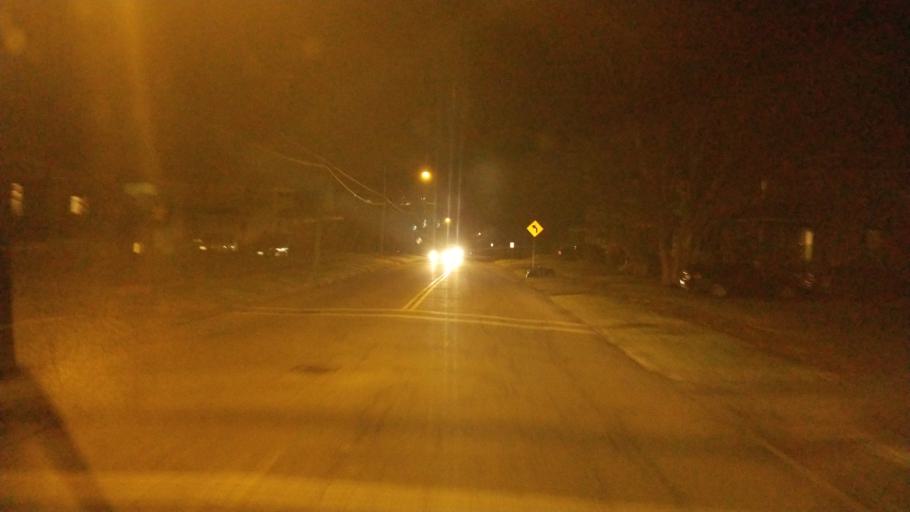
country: US
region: Ohio
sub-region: Carroll County
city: Carrollton
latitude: 40.5701
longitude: -81.0889
